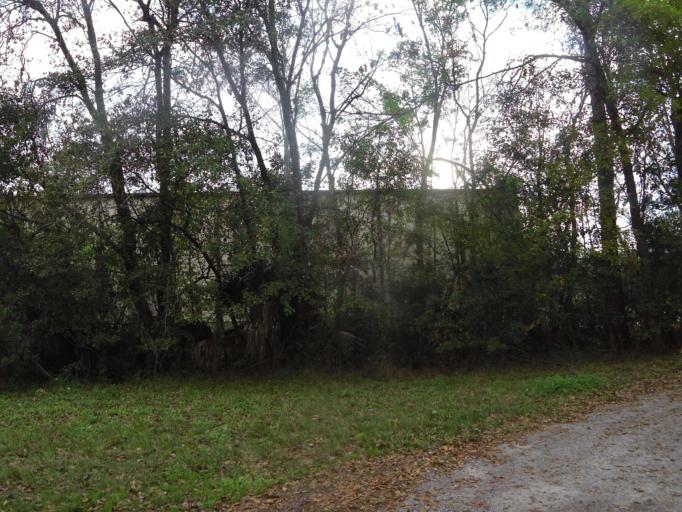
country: US
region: Florida
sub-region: Duval County
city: Jacksonville
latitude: 30.2616
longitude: -81.6194
